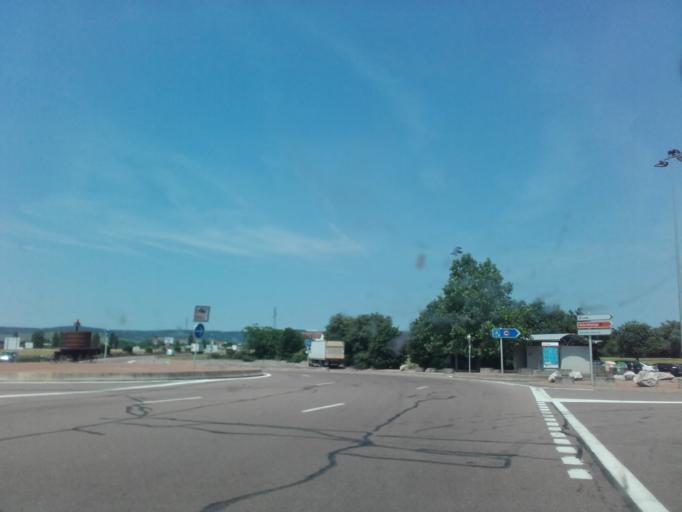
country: FR
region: Bourgogne
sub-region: Departement de la Cote-d'Or
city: Bligny-les-Beaune
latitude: 47.0029
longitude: 4.8545
